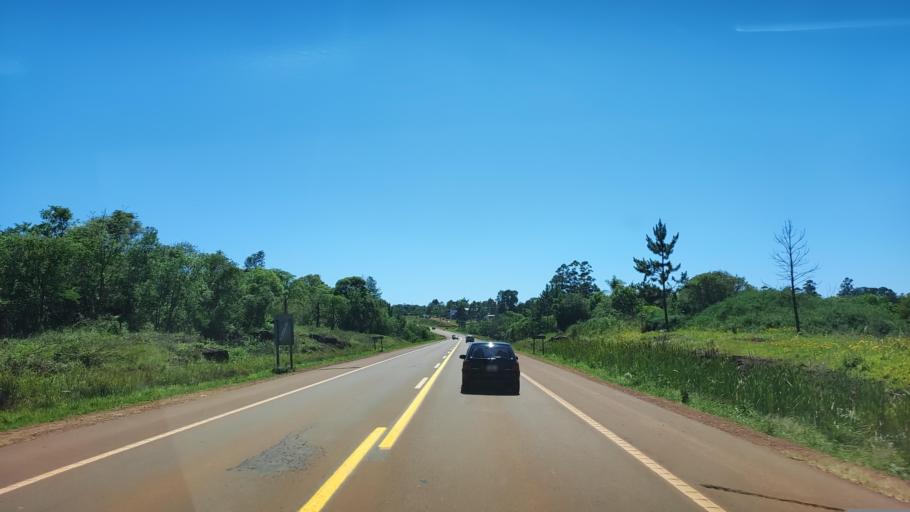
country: AR
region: Misiones
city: Aristobulo del Valle
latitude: -27.0996
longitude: -54.8798
